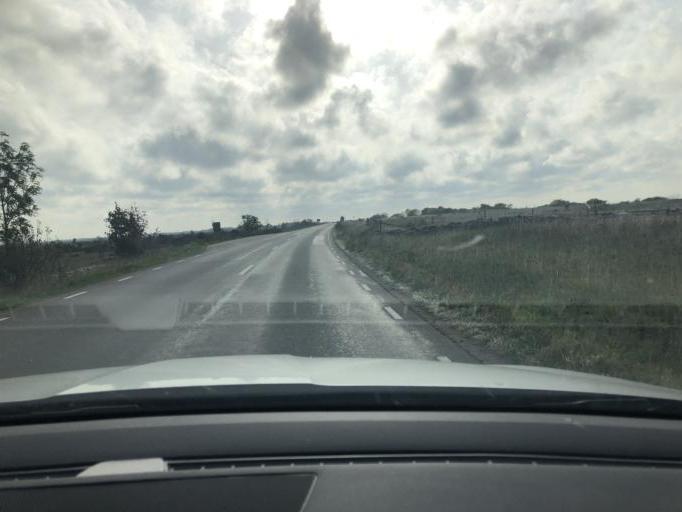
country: SE
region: Kalmar
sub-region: Morbylanga Kommun
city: Moerbylanga
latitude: 56.3869
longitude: 16.4347
